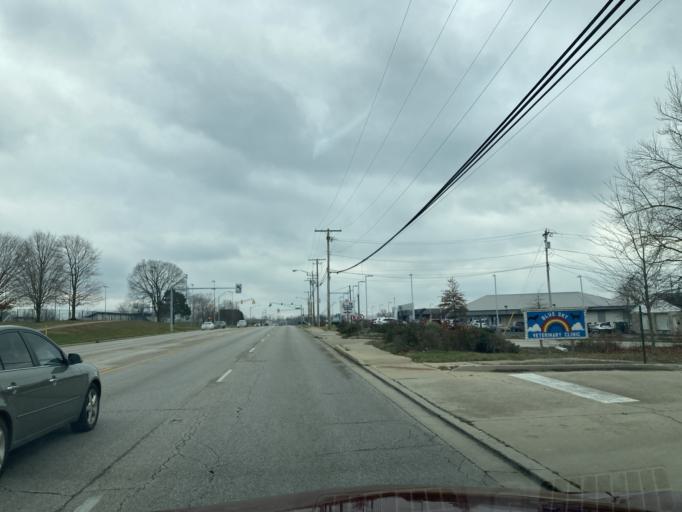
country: US
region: Indiana
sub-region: Monroe County
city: Bloomington
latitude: 39.1434
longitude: -86.5317
